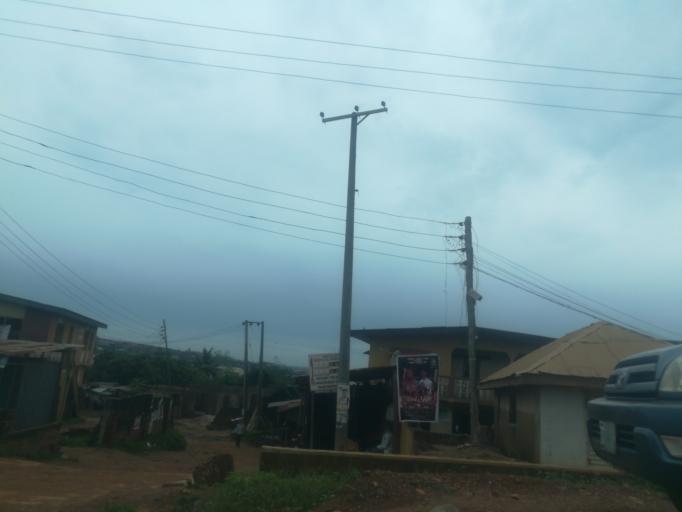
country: NG
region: Oyo
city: Ibadan
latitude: 7.3896
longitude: 3.9529
